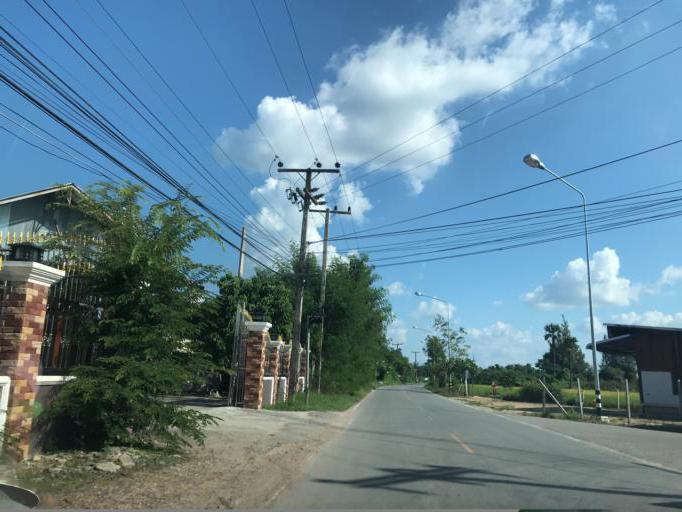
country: TH
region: Chiang Mai
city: Doi Lo
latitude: 18.5353
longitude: 98.8409
